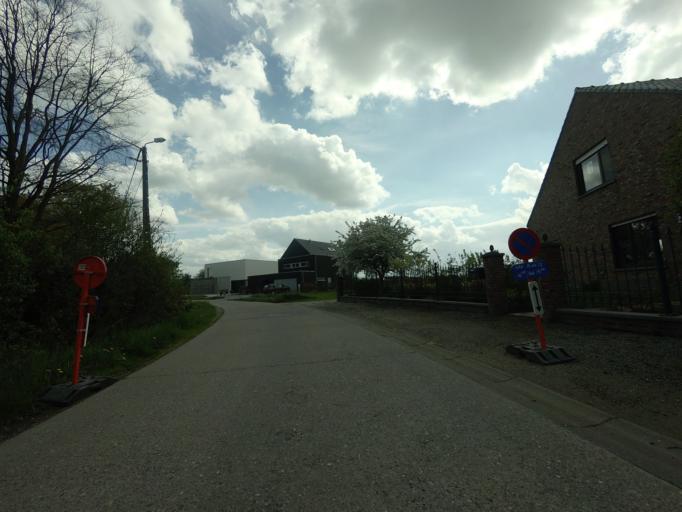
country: BE
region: Flanders
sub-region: Provincie Vlaams-Brabant
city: Kapelle-op-den-Bos
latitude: 51.0278
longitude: 4.4070
